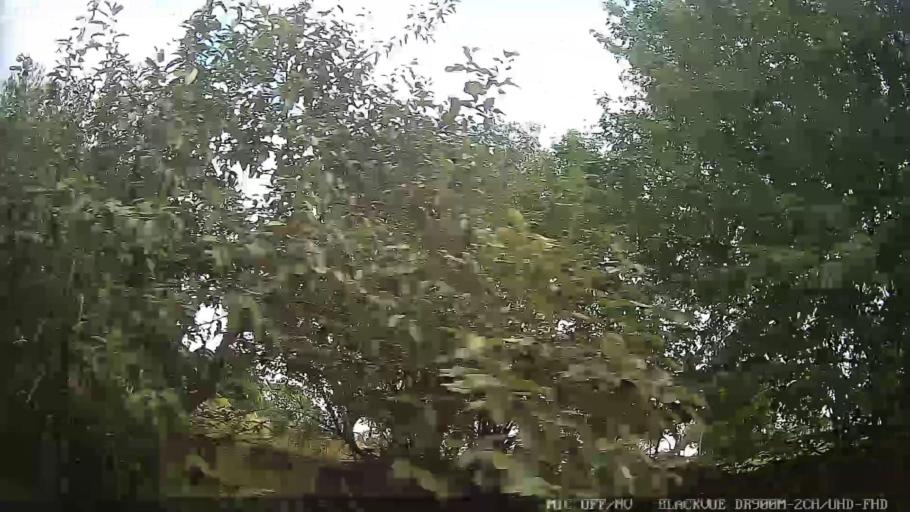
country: BR
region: Sao Paulo
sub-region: Indaiatuba
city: Indaiatuba
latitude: -23.1502
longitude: -47.1569
